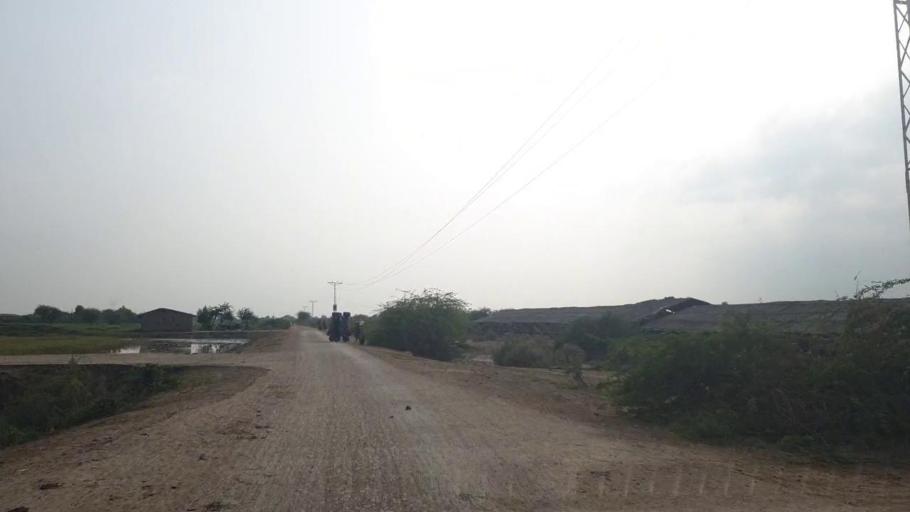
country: PK
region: Sindh
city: Badin
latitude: 24.6222
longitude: 68.6884
